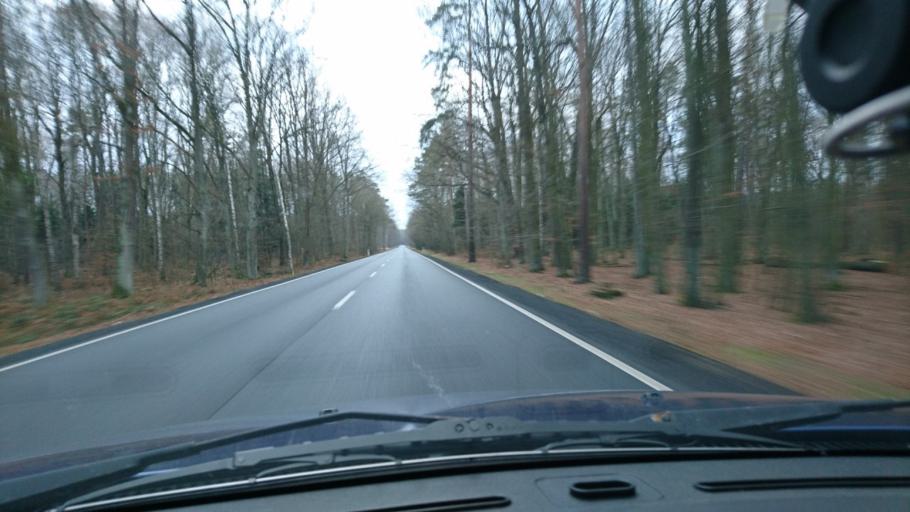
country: PL
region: Opole Voivodeship
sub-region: Powiat oleski
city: Olesno
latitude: 50.9287
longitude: 18.3349
